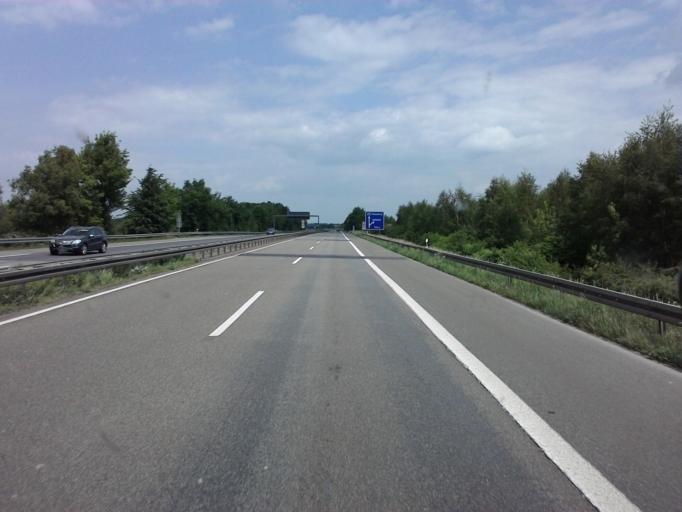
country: DE
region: North Rhine-Westphalia
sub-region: Regierungsbezirk Dusseldorf
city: Kamp-Lintfort
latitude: 51.5051
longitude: 6.5797
